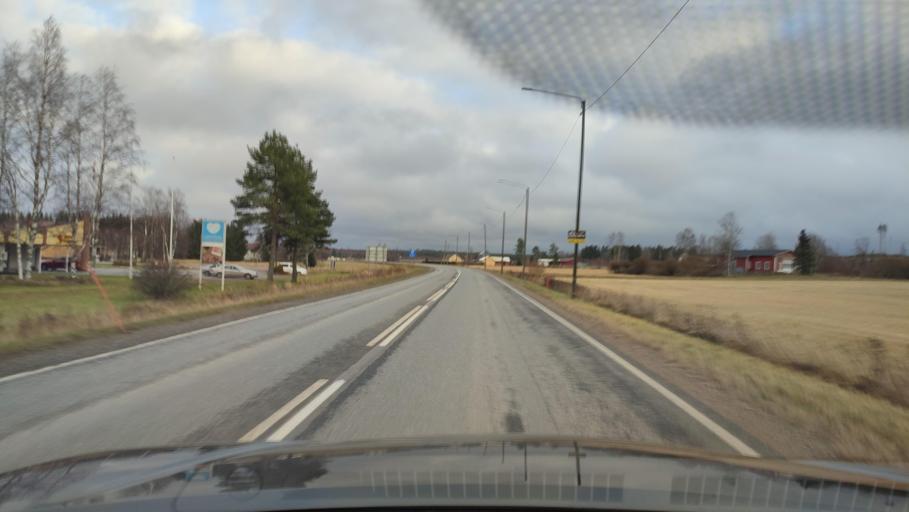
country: FI
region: Southern Ostrobothnia
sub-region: Suupohja
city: Kauhajoki
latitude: 62.3563
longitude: 22.0631
